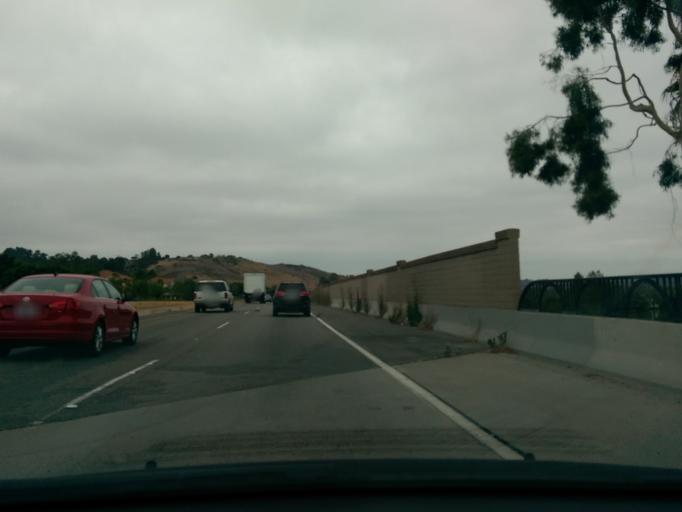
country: US
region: California
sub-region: San Diego County
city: Camp Pendleton South
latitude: 33.2301
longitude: -117.3136
